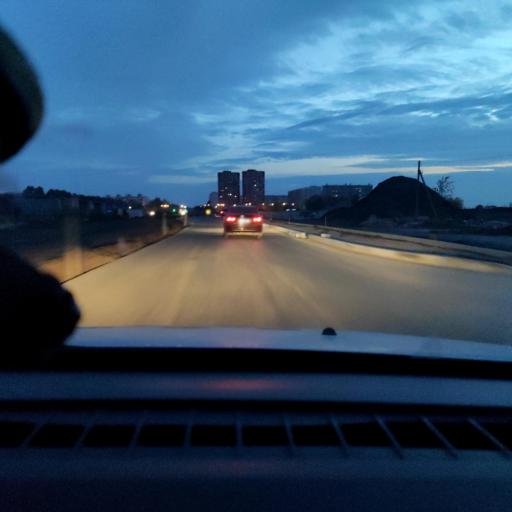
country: RU
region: Samara
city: Samara
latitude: 53.1009
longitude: 50.0768
